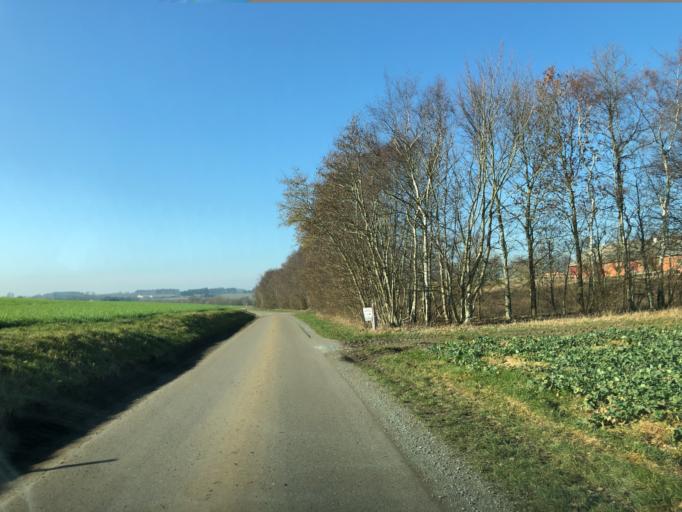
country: DK
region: Central Jutland
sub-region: Silkeborg Kommune
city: Svejbaek
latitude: 56.1966
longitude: 9.7132
